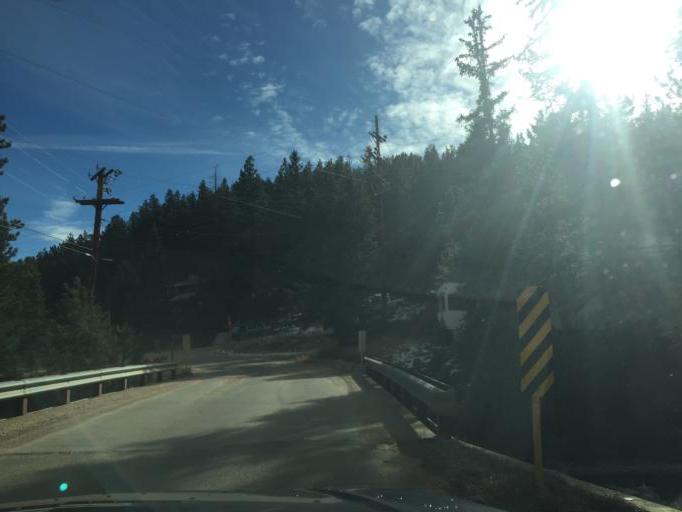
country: US
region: Colorado
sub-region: Jefferson County
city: Evergreen
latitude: 39.4063
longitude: -105.4865
